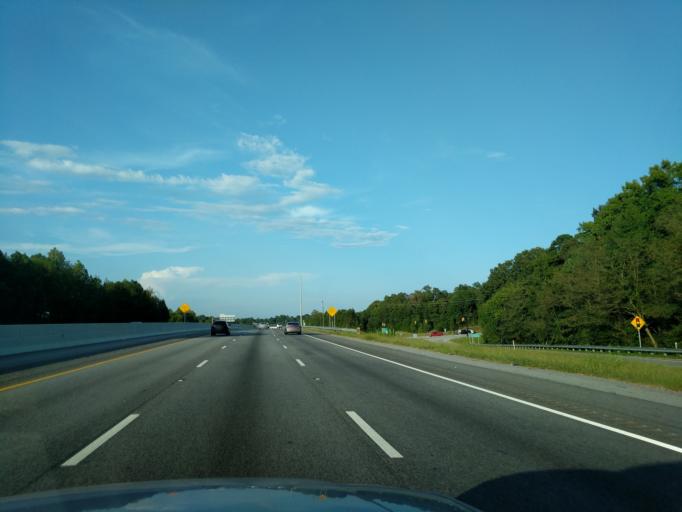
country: US
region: South Carolina
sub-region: Greenville County
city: Mauldin
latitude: 34.7629
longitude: -82.2806
